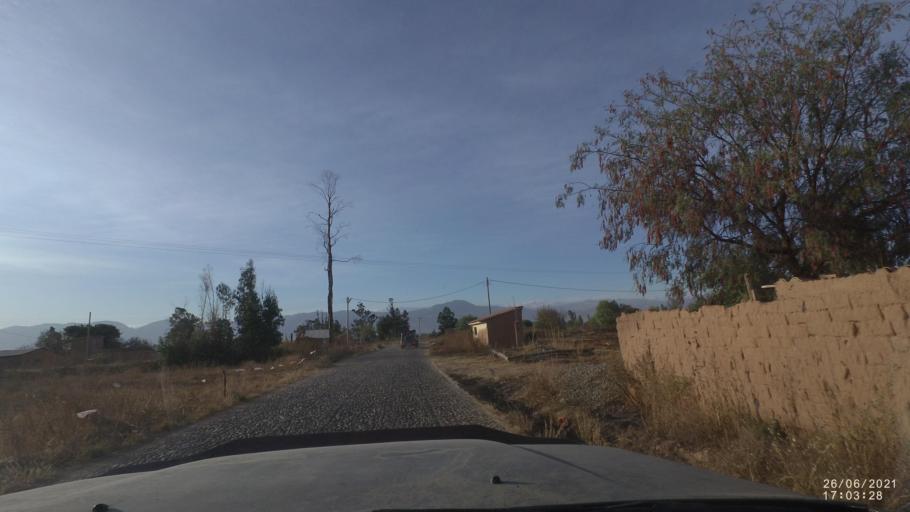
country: BO
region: Cochabamba
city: Cliza
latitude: -17.6422
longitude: -65.9118
